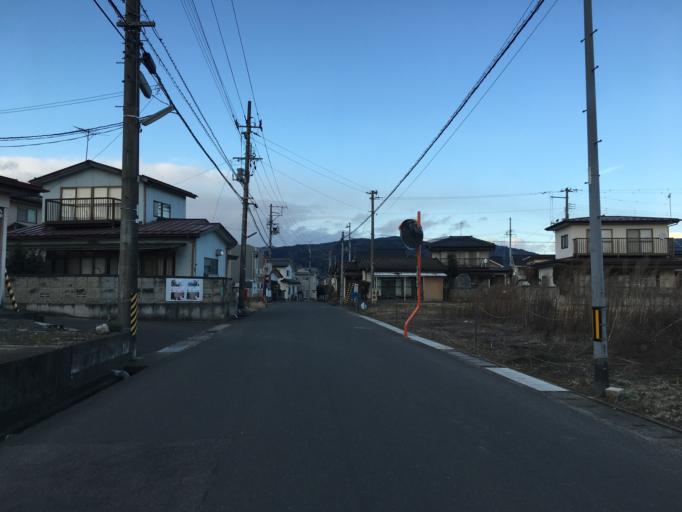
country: JP
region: Fukushima
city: Hobaramachi
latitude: 37.8079
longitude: 140.4899
